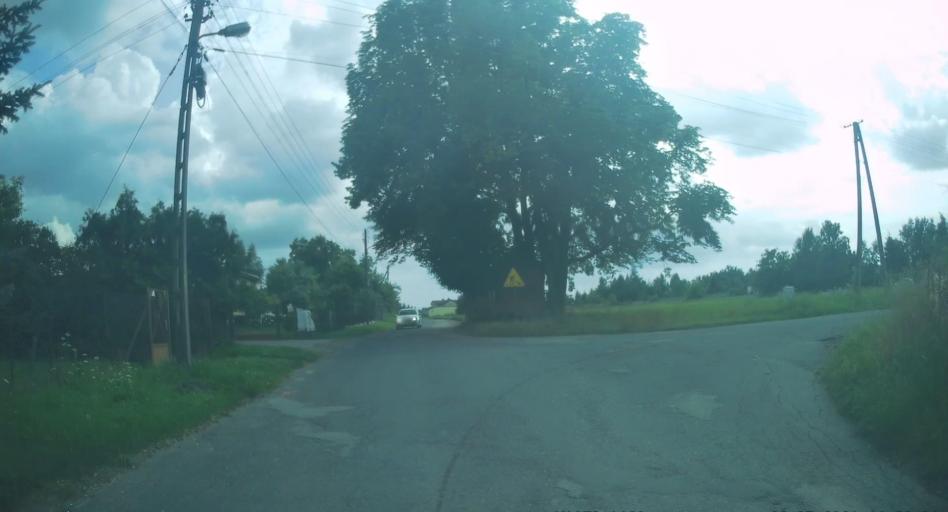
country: PL
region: Lodz Voivodeship
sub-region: Powiat brzezinski
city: Rogow
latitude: 51.8176
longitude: 19.8975
